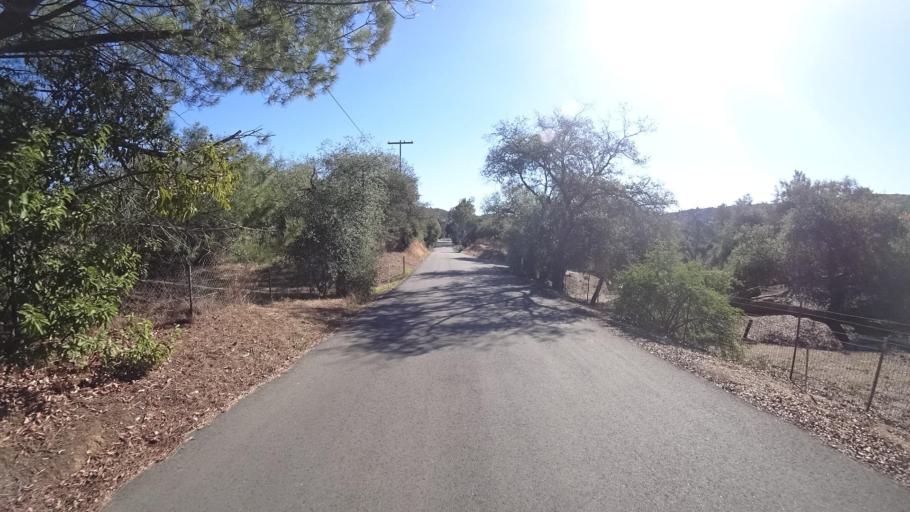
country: US
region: California
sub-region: San Diego County
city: Jamul
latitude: 32.6780
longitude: -116.7310
